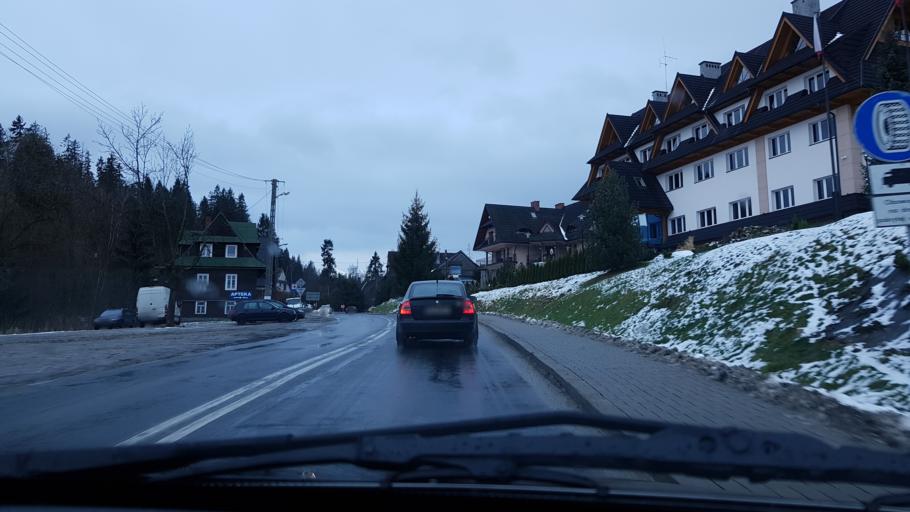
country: PL
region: Lesser Poland Voivodeship
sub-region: Powiat tatrzanski
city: Czarna Gora
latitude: 49.3568
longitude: 20.1250
